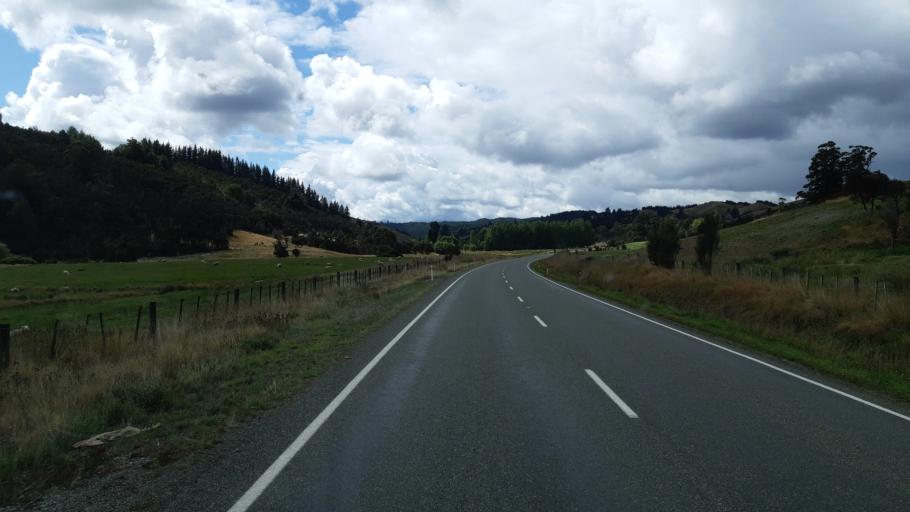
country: NZ
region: Tasman
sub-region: Tasman District
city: Wakefield
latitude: -41.6414
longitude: 172.6658
